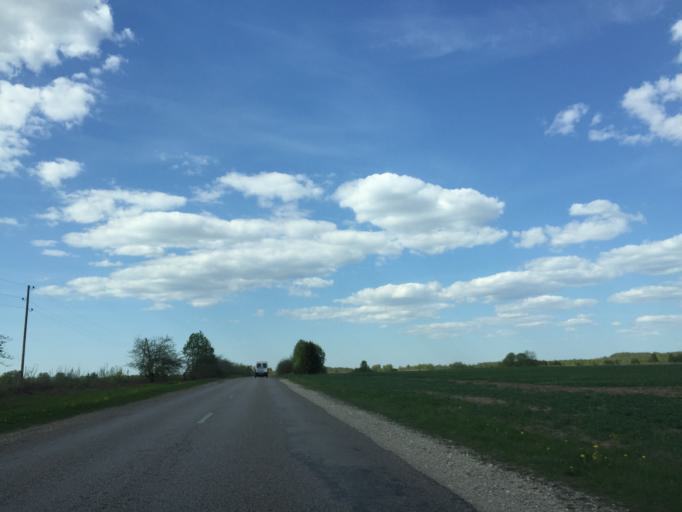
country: LV
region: Limbazu Rajons
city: Limbazi
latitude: 57.4576
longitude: 24.7212
